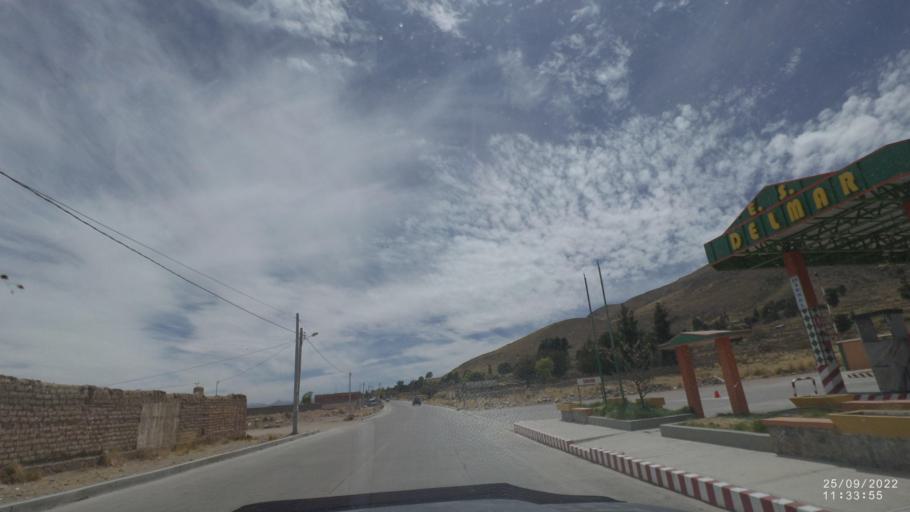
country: BO
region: Oruro
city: Challapata
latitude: -19.0076
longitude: -66.7760
